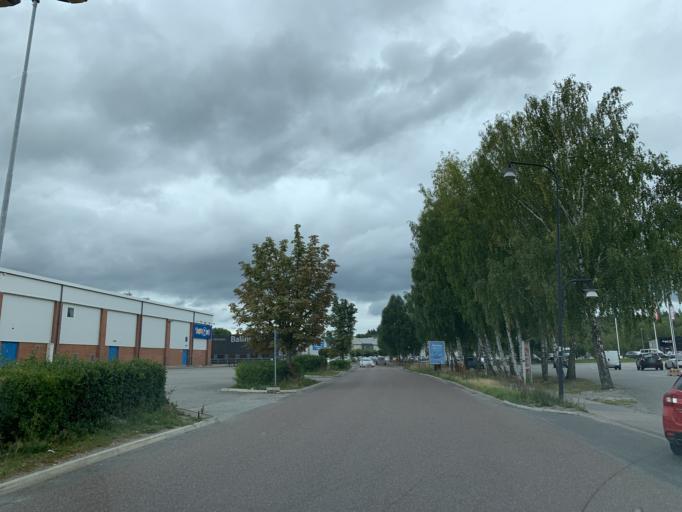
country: SE
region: Stockholm
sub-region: Huddinge Kommun
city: Segeltorp
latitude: 59.2686
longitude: 17.9208
